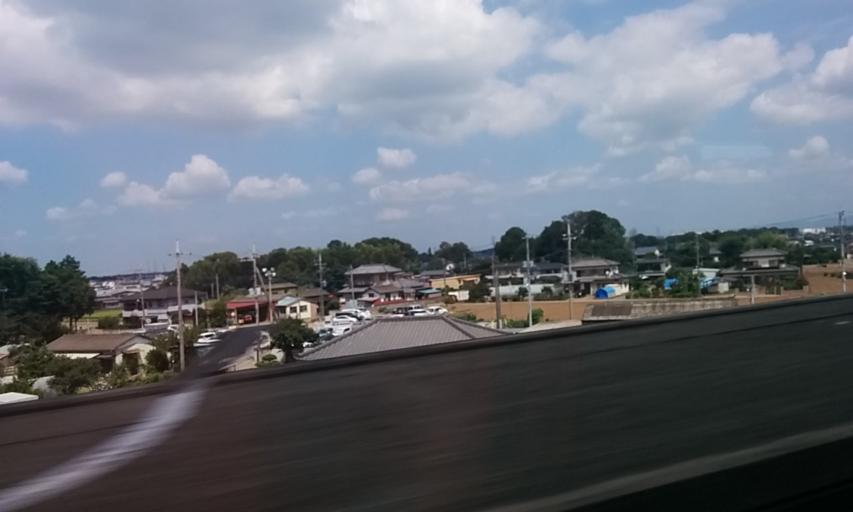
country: JP
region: Ibaraki
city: Koga
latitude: 36.1594
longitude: 139.7303
